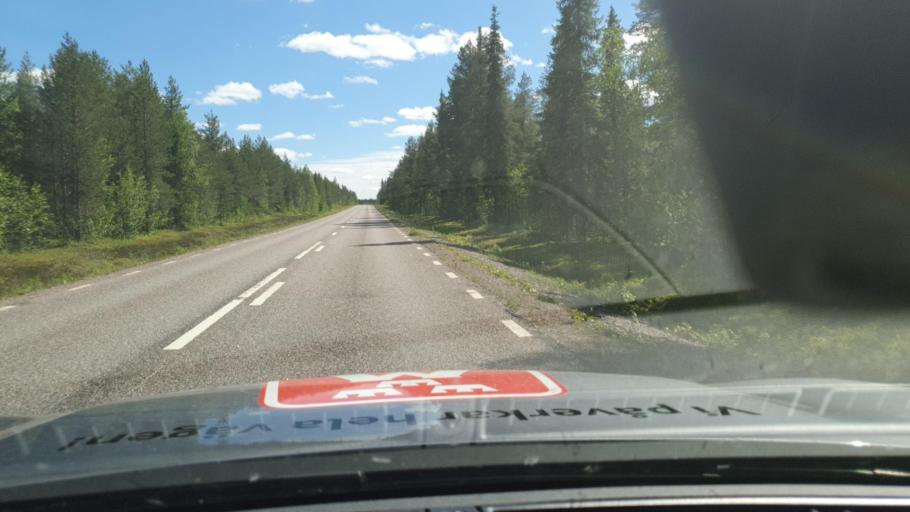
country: SE
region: Norrbotten
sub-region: Pajala Kommun
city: Pajala
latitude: 67.1754
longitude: 23.5050
